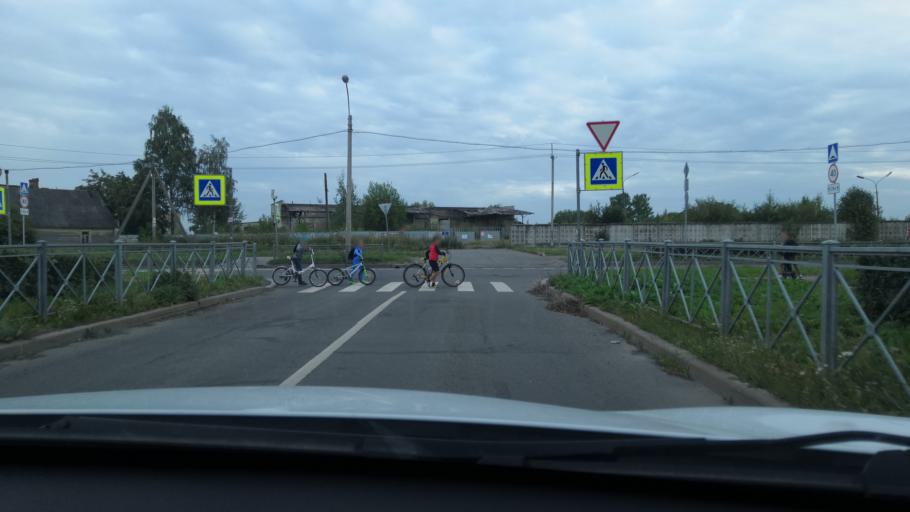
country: RU
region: St.-Petersburg
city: Pushkin
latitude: 59.7008
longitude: 30.3885
